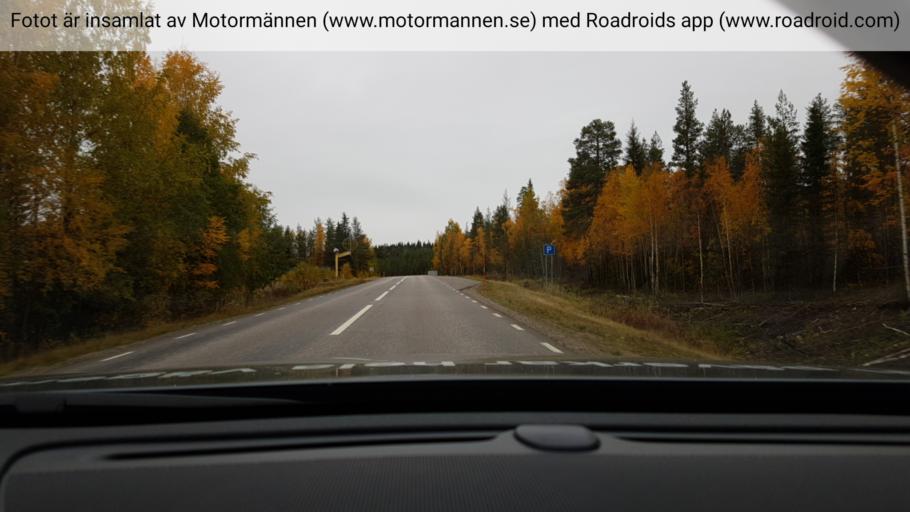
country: SE
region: Norrbotten
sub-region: Overkalix Kommun
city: OEverkalix
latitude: 66.5498
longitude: 22.7575
